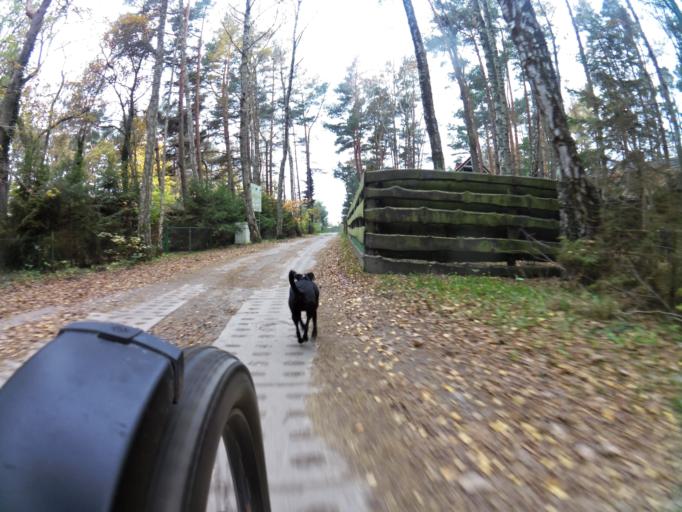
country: PL
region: Pomeranian Voivodeship
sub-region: Powiat pucki
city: Krokowa
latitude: 54.8289
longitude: 18.0965
